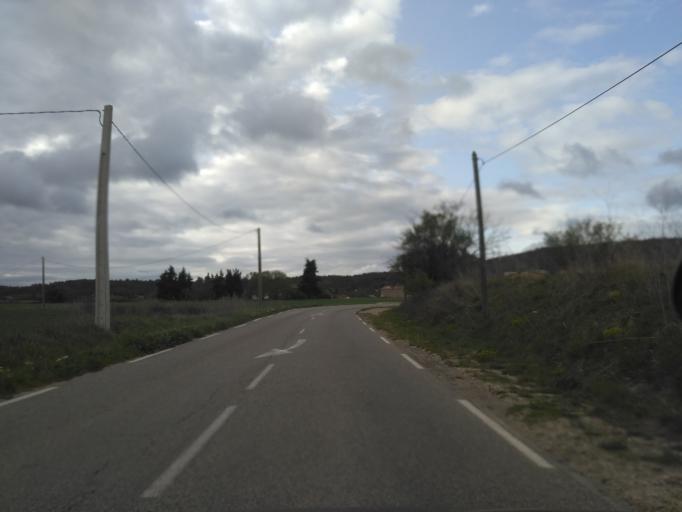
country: FR
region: Provence-Alpes-Cote d'Azur
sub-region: Departement du Var
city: Barjols
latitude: 43.5877
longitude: 6.0134
